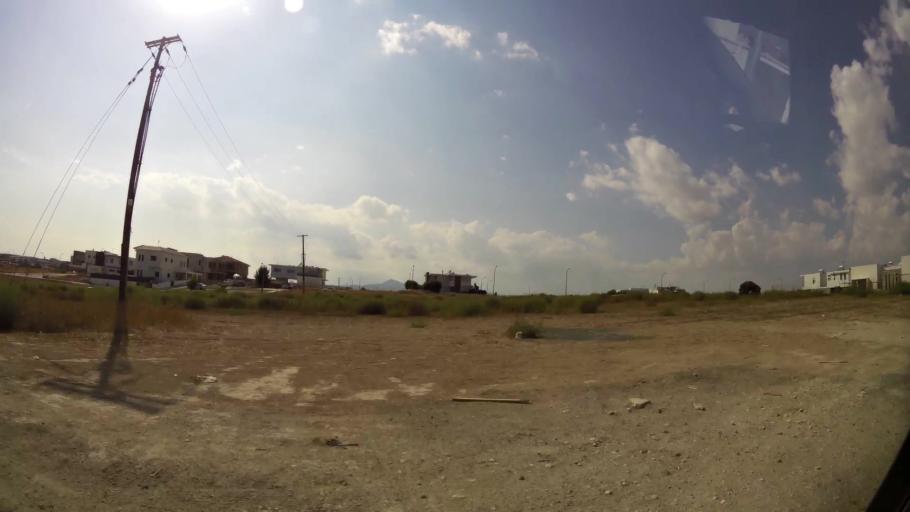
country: CY
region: Larnaka
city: Dhromolaxia
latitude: 34.9066
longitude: 33.5814
